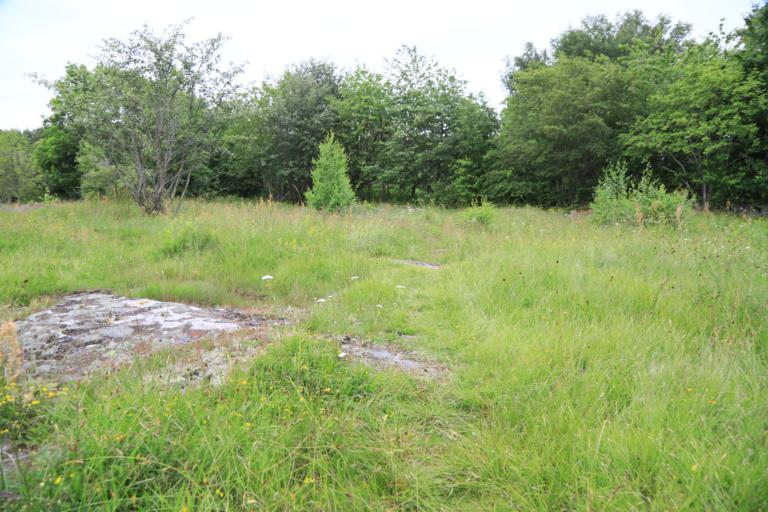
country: SE
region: Halland
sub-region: Varbergs Kommun
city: Traslovslage
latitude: 57.1041
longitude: 12.3036
